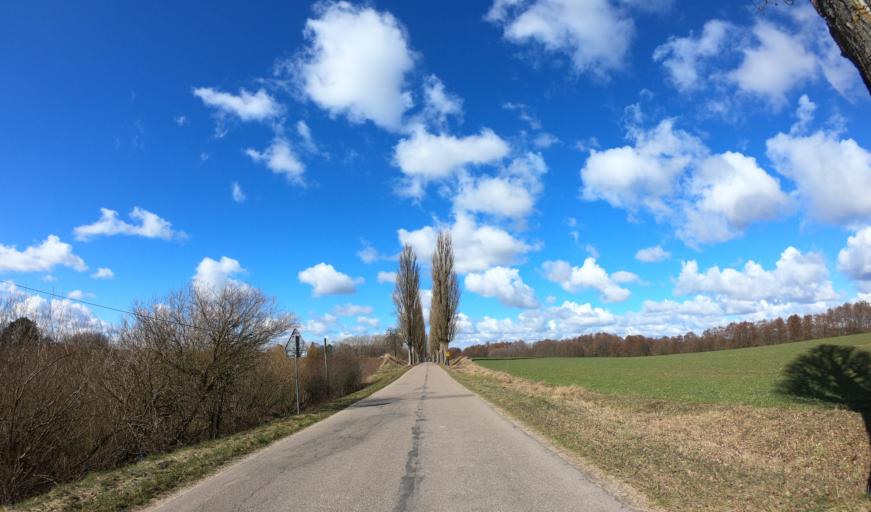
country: PL
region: West Pomeranian Voivodeship
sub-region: Powiat drawski
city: Drawsko Pomorskie
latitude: 53.4863
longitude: 15.8722
